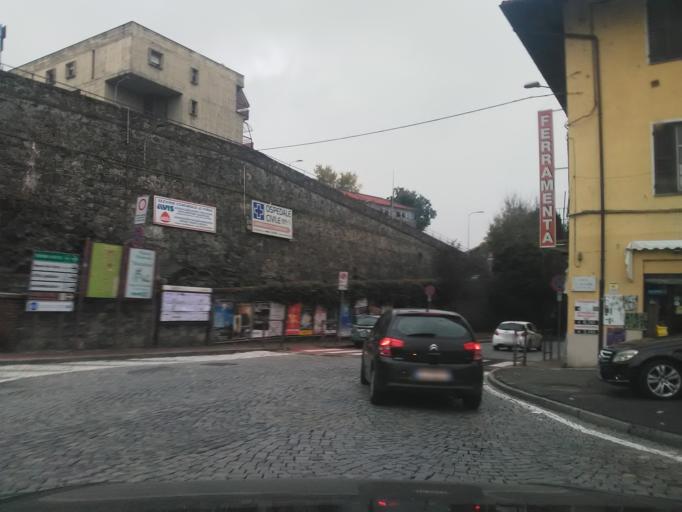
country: IT
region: Piedmont
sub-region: Provincia di Torino
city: Ivrea
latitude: 45.4672
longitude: 7.8718
